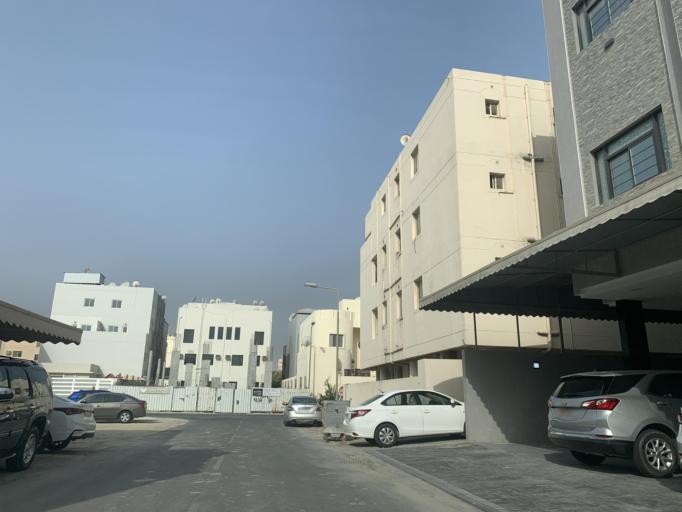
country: BH
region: Northern
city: Madinat `Isa
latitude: 26.1891
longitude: 50.5634
